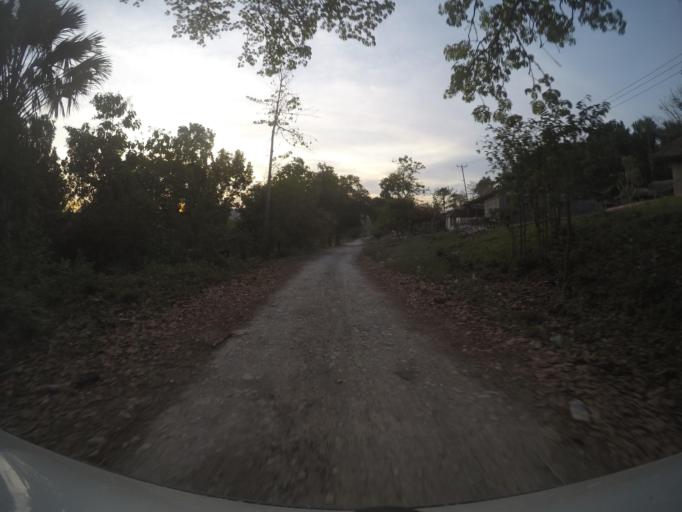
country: TL
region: Viqueque
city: Viqueque
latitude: -8.9241
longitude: 126.3993
